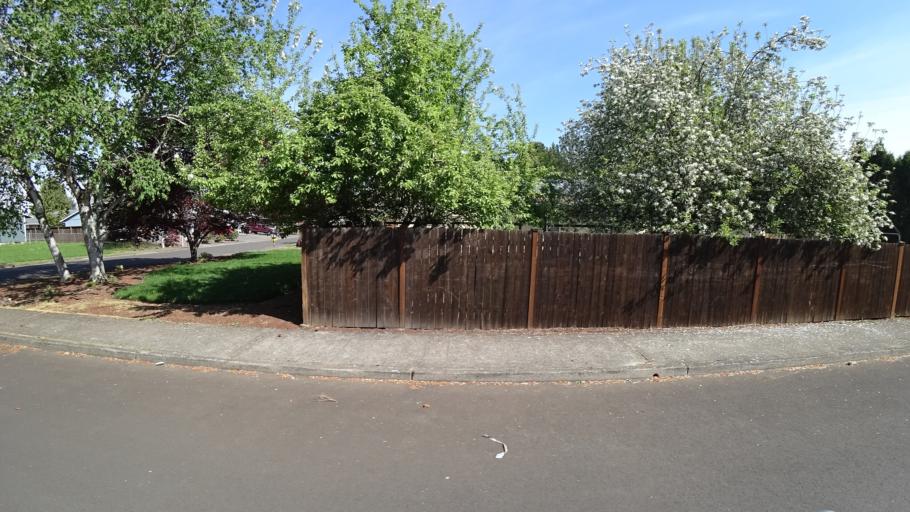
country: US
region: Oregon
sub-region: Washington County
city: Hillsboro
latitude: 45.5268
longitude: -122.9405
